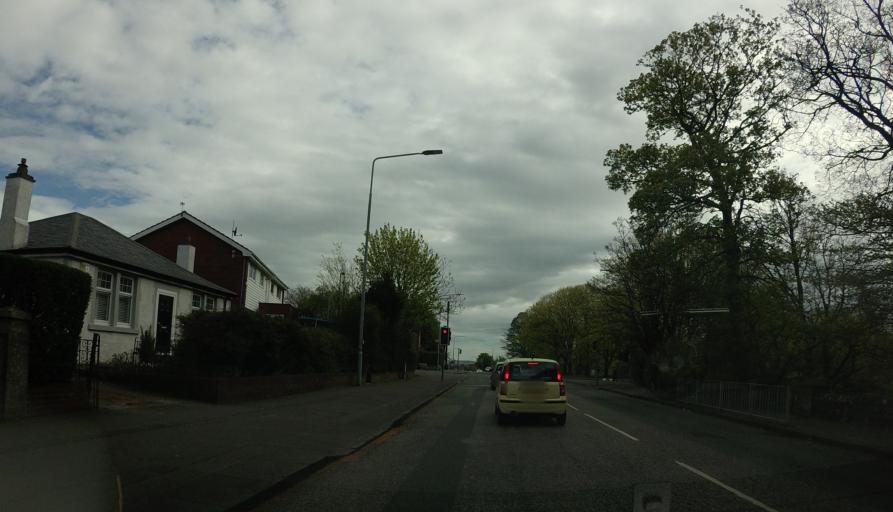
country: GB
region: Scotland
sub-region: West Lothian
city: Broxburn
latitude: 55.9317
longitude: -3.4989
